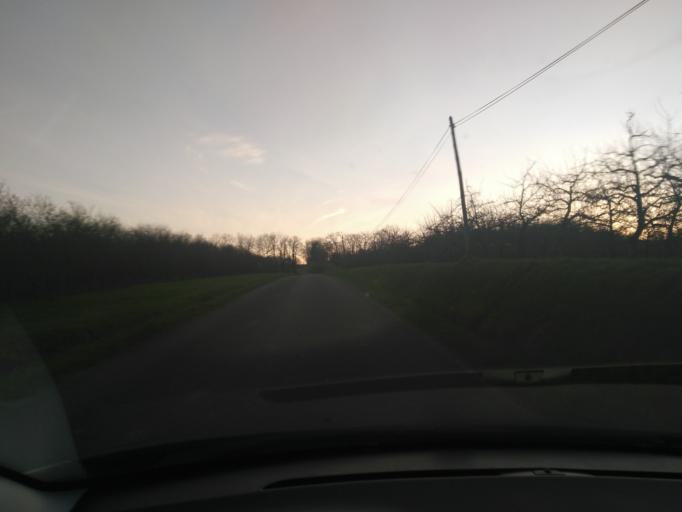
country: FR
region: Aquitaine
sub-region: Departement du Lot-et-Garonne
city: Saint-Hilaire
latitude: 44.5370
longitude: 0.6971
